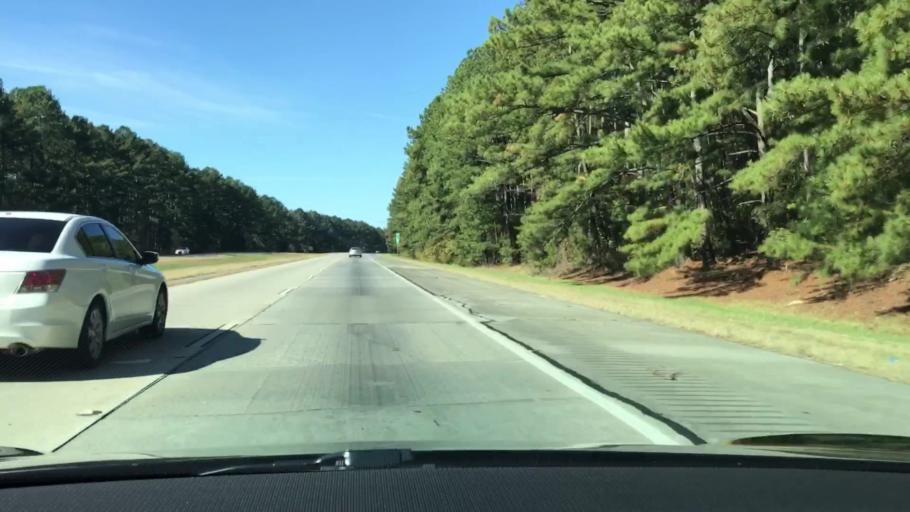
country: US
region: Georgia
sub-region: Taliaferro County
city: Crawfordville
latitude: 33.5314
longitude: -82.9814
